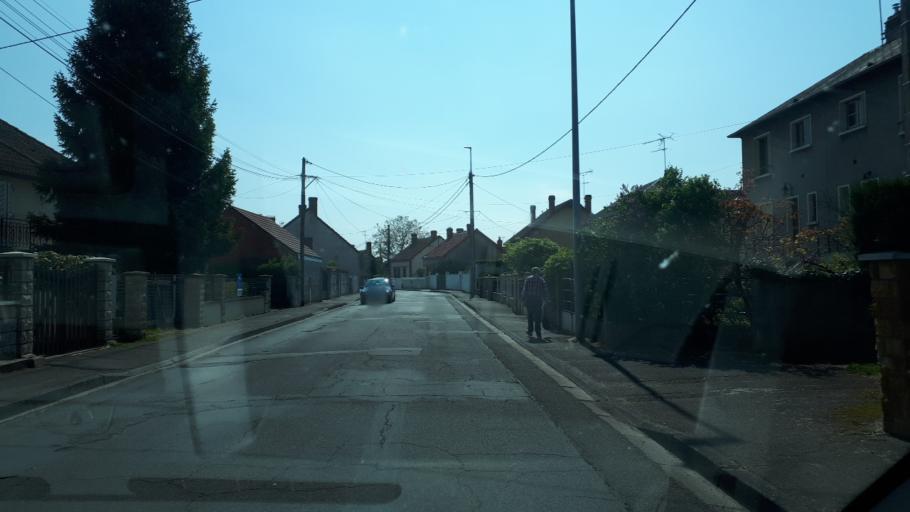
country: FR
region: Centre
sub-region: Departement du Loir-et-Cher
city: Romorantin-Lanthenay
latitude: 47.3601
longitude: 1.7507
